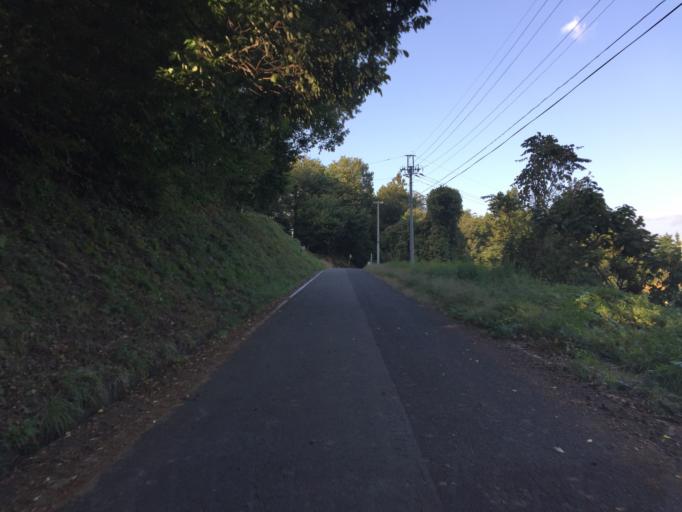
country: JP
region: Fukushima
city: Nihommatsu
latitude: 37.6326
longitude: 140.5619
